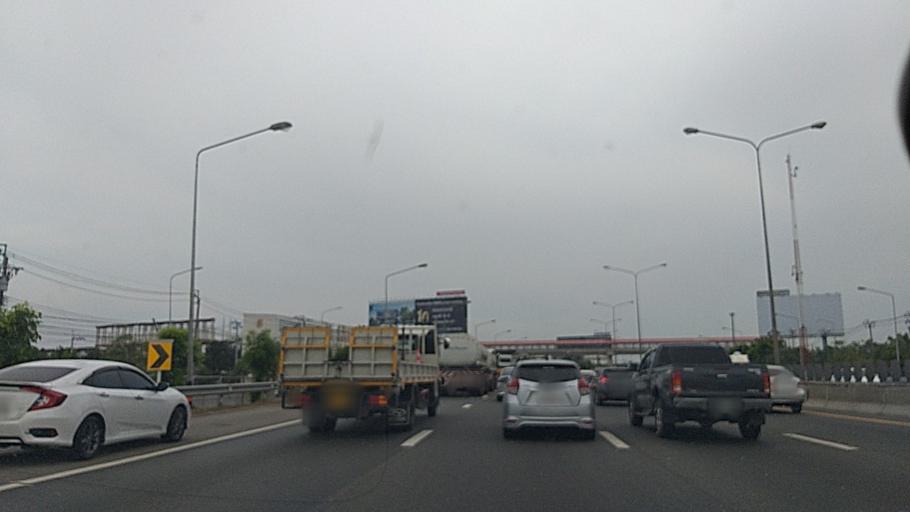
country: TH
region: Bangkok
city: Bang Na
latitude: 13.6710
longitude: 100.6993
